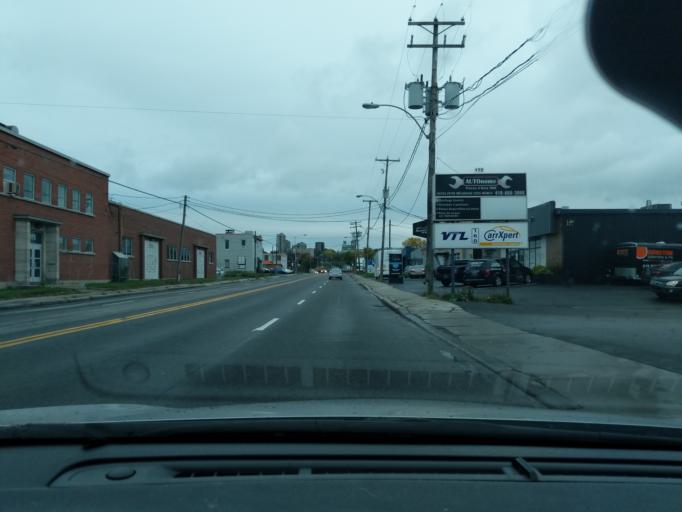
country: CA
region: Quebec
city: Quebec
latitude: 46.8057
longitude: -71.2662
